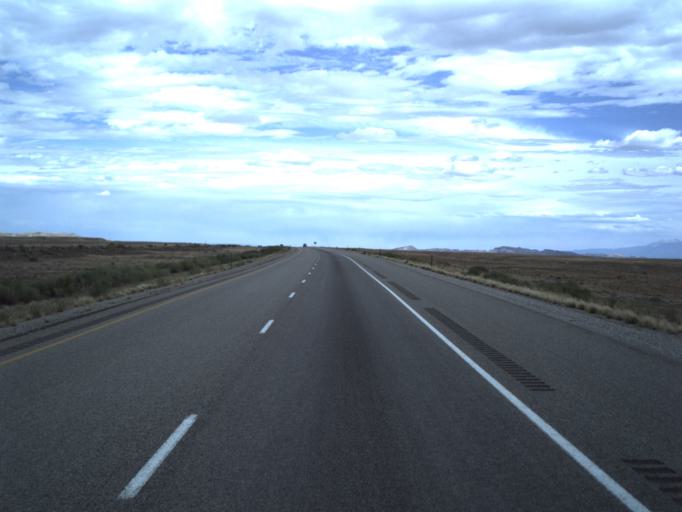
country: US
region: Utah
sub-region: Grand County
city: Moab
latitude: 38.9230
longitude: -109.9726
